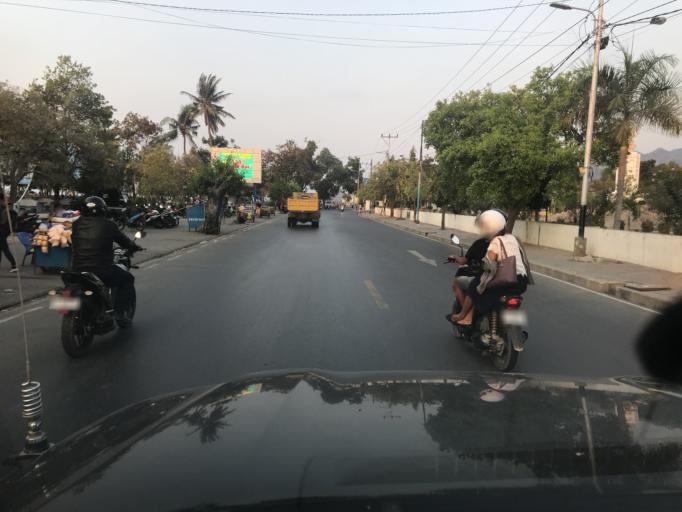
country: TL
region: Dili
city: Dili
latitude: -8.5501
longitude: 125.5844
